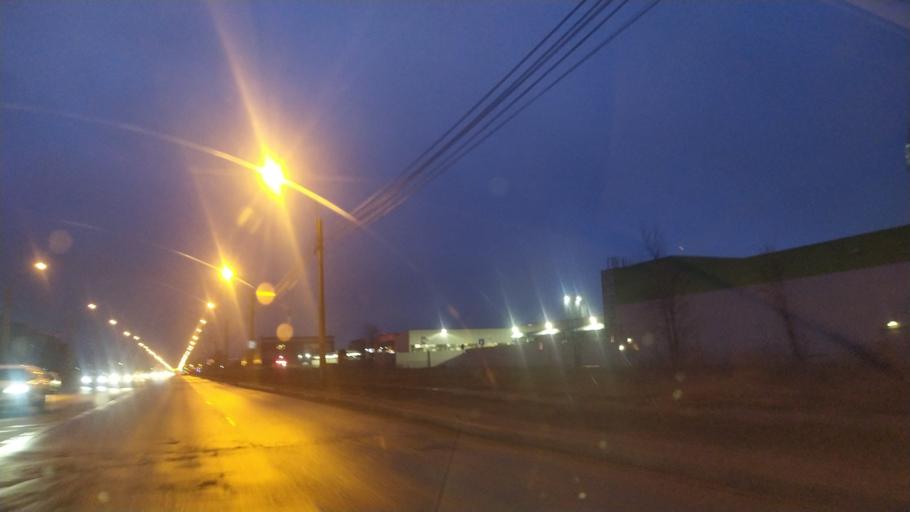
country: RU
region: Leningrad
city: Parnas
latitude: 60.0670
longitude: 30.3459
